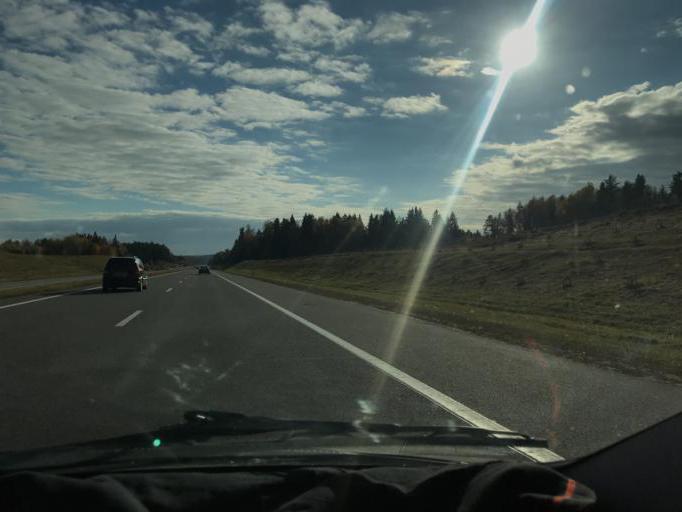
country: BY
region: Minsk
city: Lahoysk
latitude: 54.1431
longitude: 27.8094
